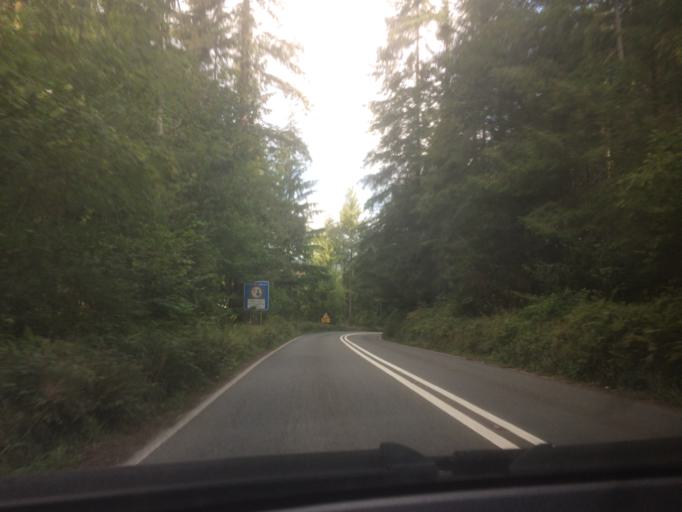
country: GB
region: England
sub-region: Cornwall
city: Gunnislake
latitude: 50.5269
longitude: -4.2097
